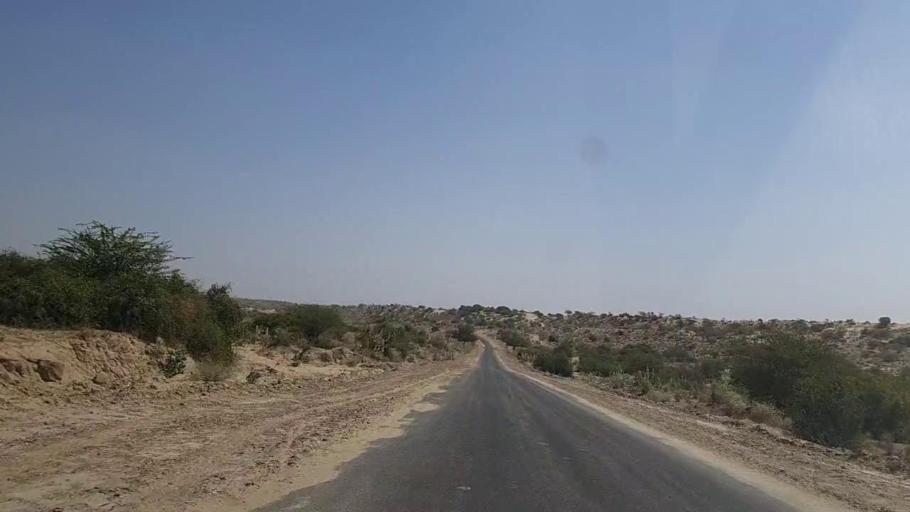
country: PK
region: Sindh
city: Diplo
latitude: 24.4818
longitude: 69.4814
